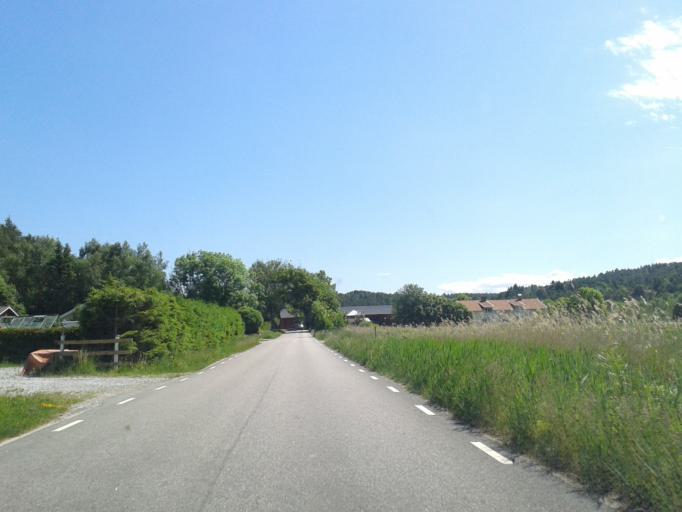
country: SE
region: Vaestra Goetaland
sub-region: Stenungsunds Kommun
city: Stora Hoga
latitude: 58.0245
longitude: 11.8765
